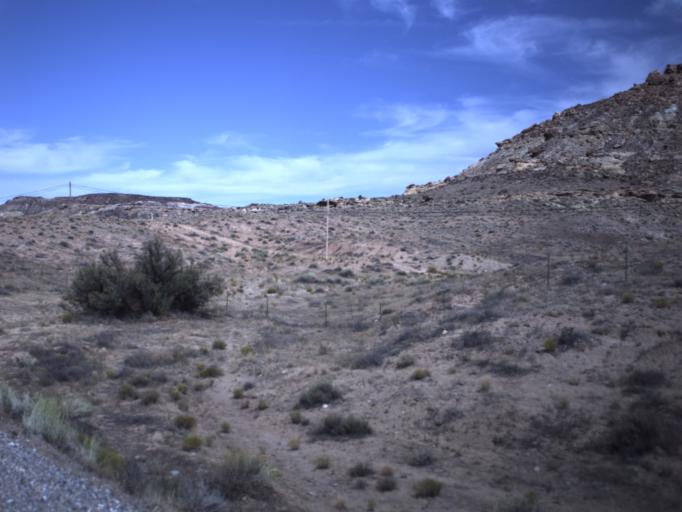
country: US
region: Colorado
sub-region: Montezuma County
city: Towaoc
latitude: 37.2126
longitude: -109.1756
